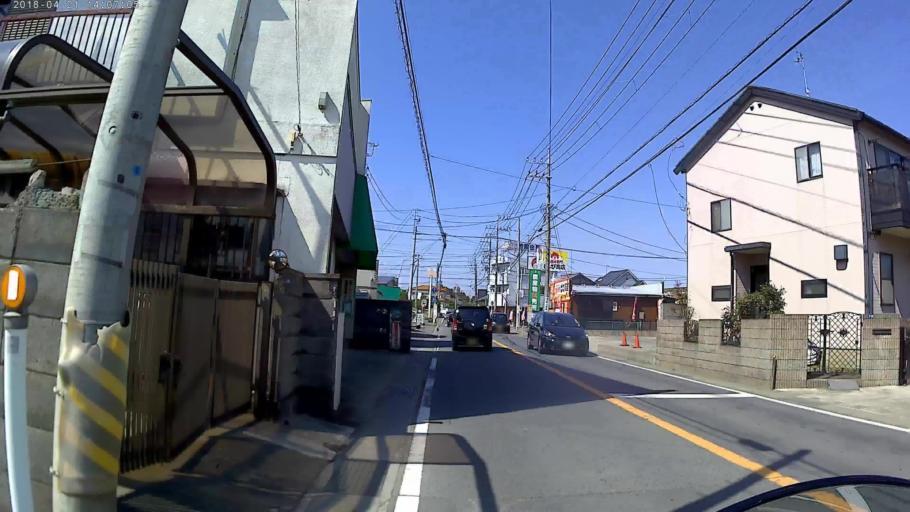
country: JP
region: Kanagawa
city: Hiratsuka
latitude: 35.3550
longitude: 139.3494
